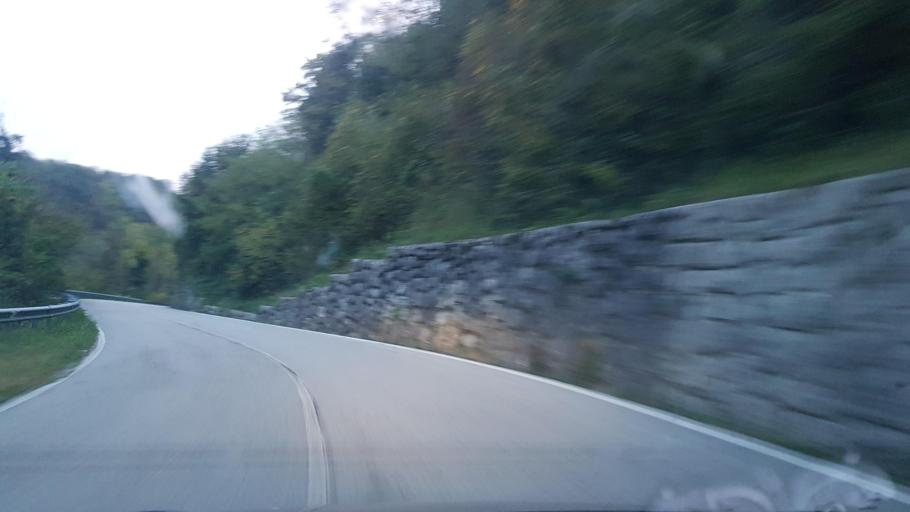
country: IT
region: Friuli Venezia Giulia
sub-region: Provincia di Pordenone
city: Anduins
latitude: 46.2292
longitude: 12.9576
